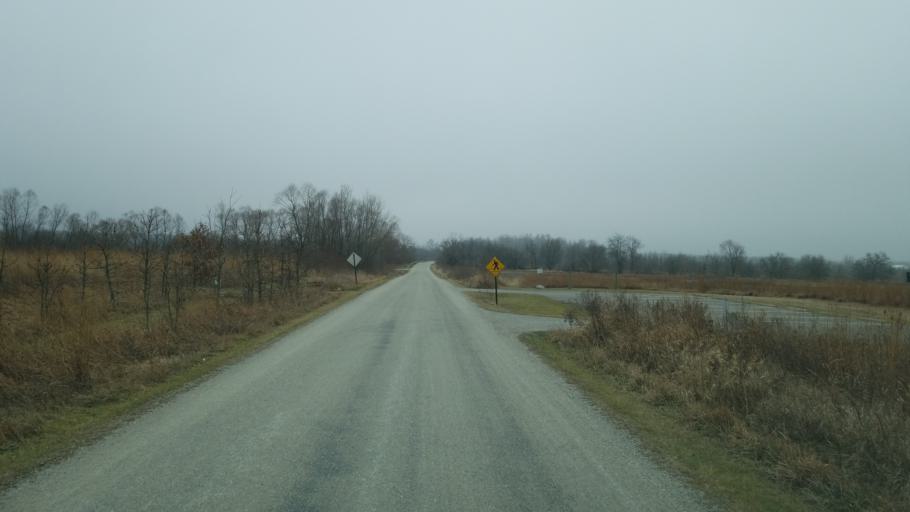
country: US
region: Indiana
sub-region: Adams County
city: Geneva
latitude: 40.5575
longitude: -85.0303
